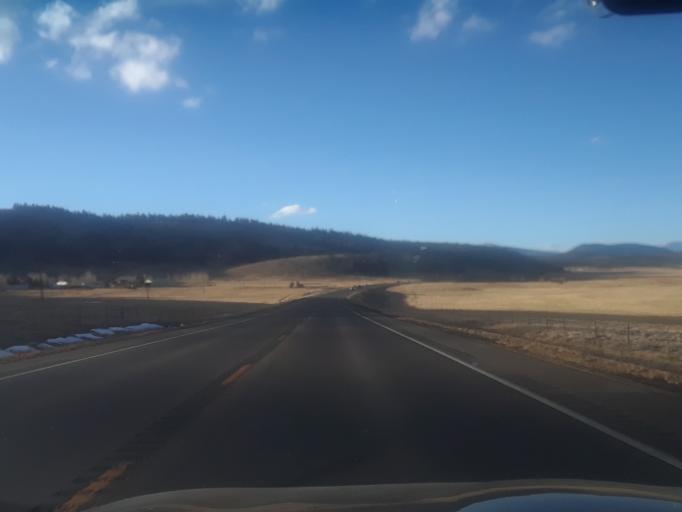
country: US
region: Colorado
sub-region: Park County
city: Fairplay
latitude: 38.9986
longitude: -105.9612
